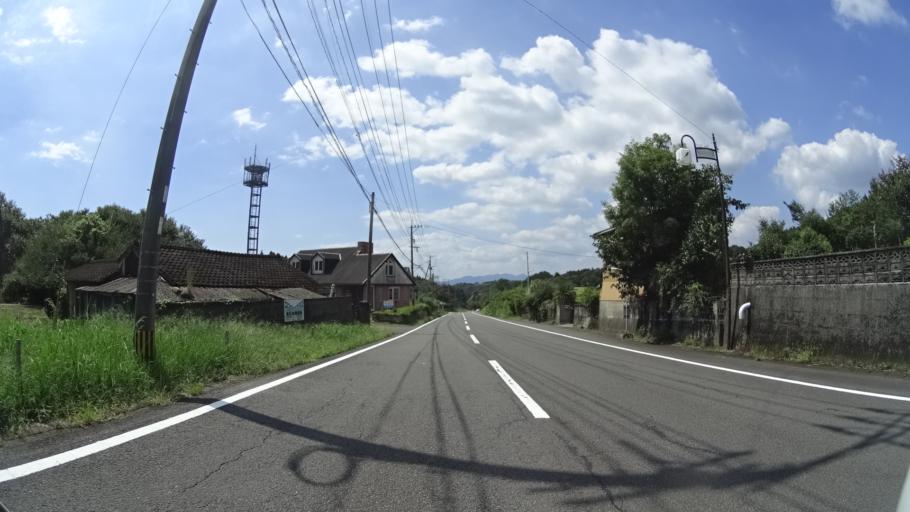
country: JP
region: Kagoshima
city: Kokubu-matsuki
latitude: 31.8613
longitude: 130.7883
